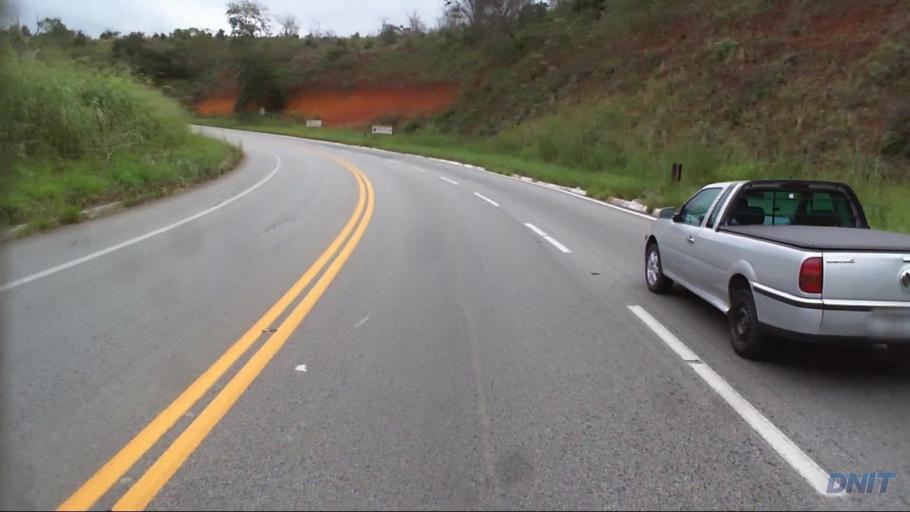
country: BR
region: Minas Gerais
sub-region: Nova Era
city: Nova Era
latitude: -19.8024
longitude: -43.0598
